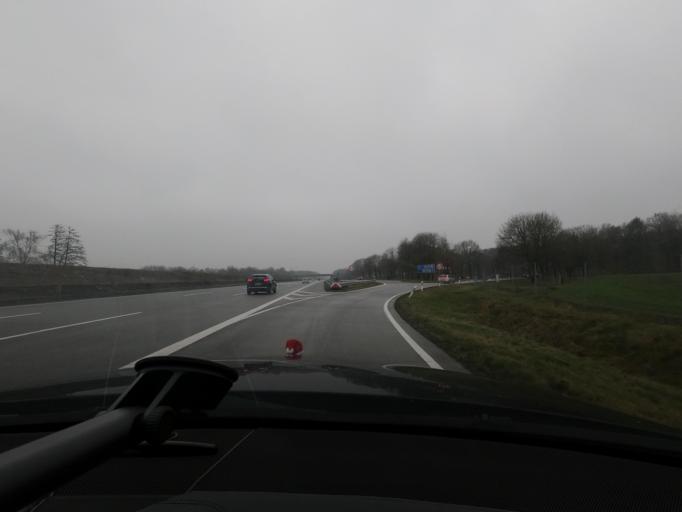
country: DE
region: Schleswig-Holstein
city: Bimohlen
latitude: 53.9429
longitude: 9.9476
